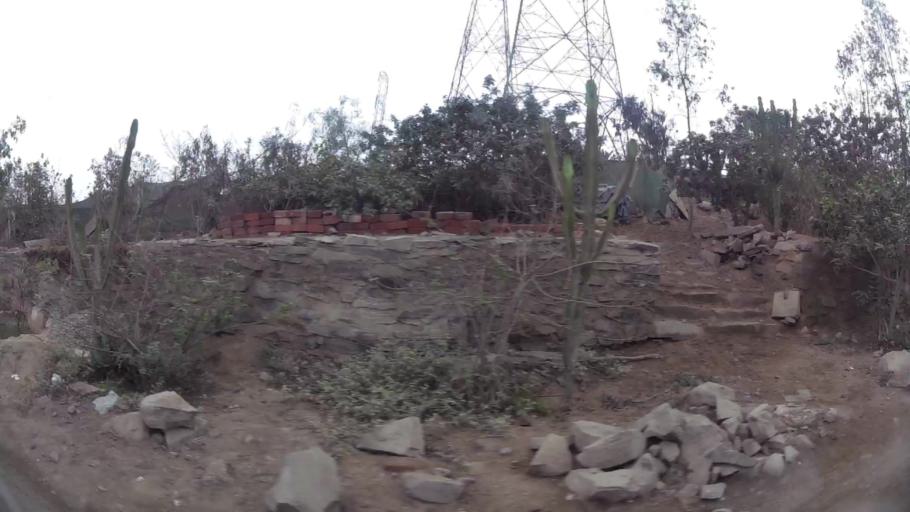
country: PE
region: Lima
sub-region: Lima
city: Surco
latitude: -12.1826
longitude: -76.9568
